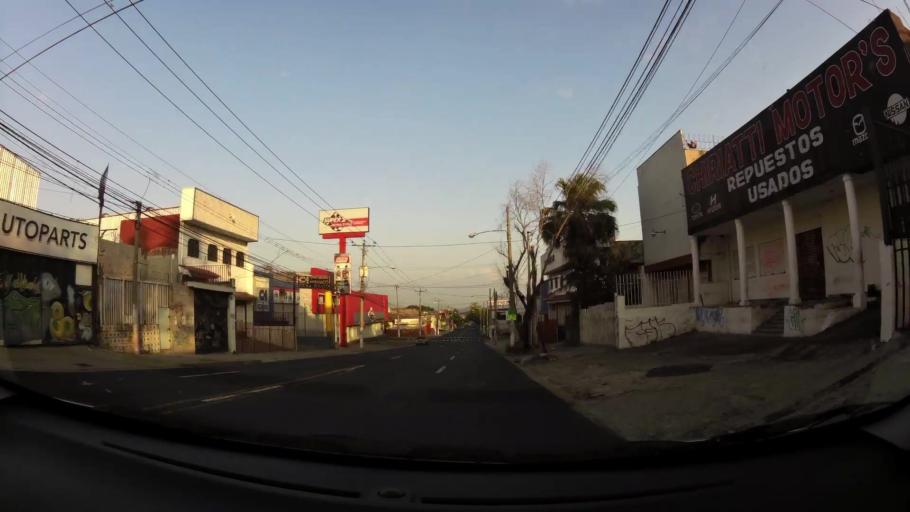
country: SV
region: San Salvador
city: San Salvador
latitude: 13.7140
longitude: -89.1995
